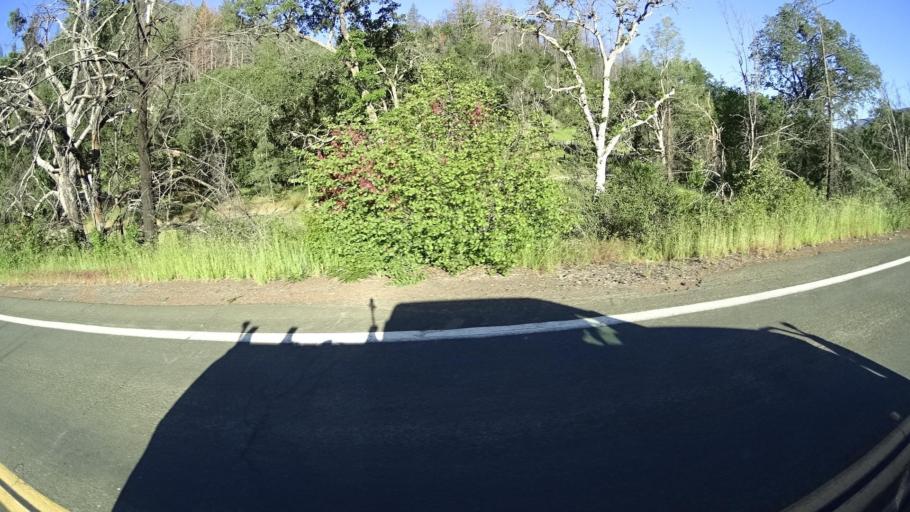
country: US
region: California
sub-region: Lake County
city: Upper Lake
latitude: 39.2499
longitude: -122.9527
